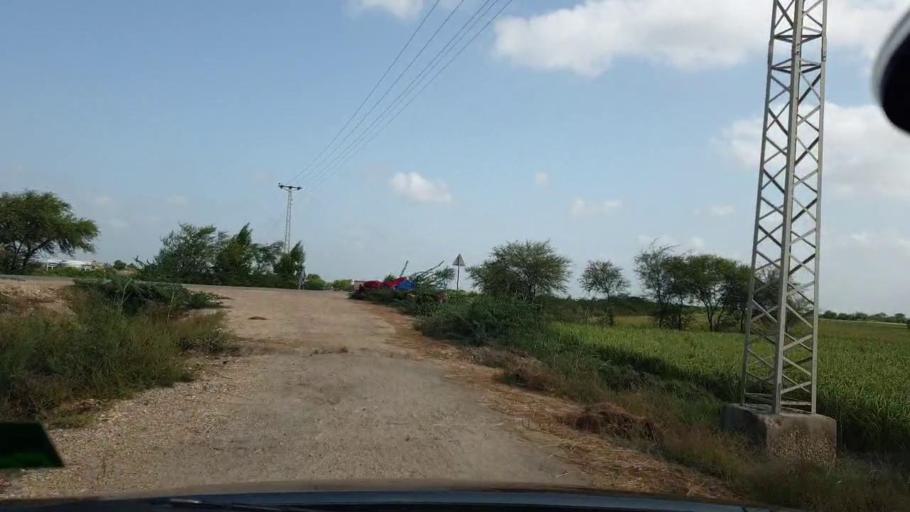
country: PK
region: Sindh
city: Kadhan
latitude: 24.6419
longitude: 69.0937
